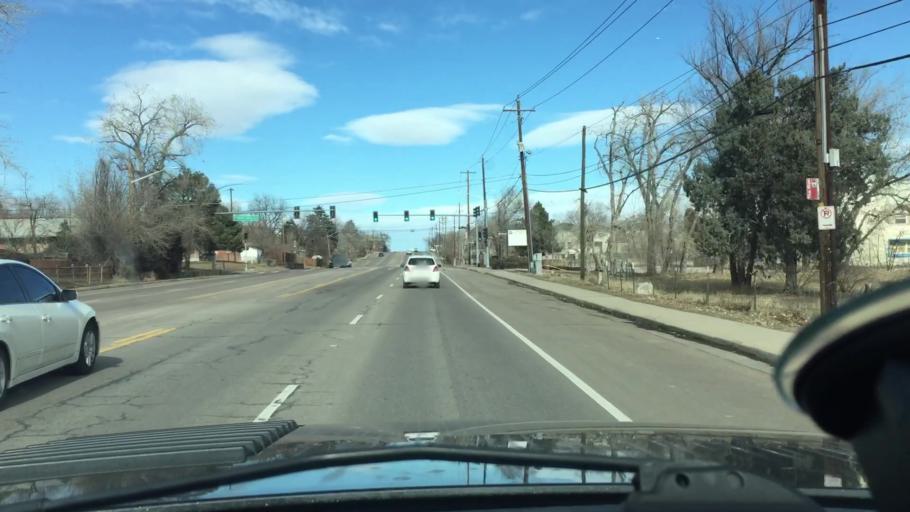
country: US
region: Colorado
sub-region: Adams County
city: Sherrelwood
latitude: 39.8412
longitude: -105.0060
